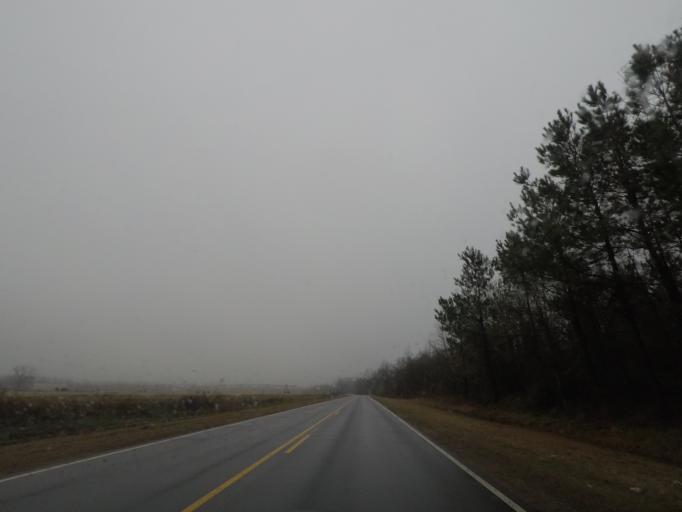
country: US
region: North Carolina
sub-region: Scotland County
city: Laurinburg
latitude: 34.7749
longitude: -79.4297
